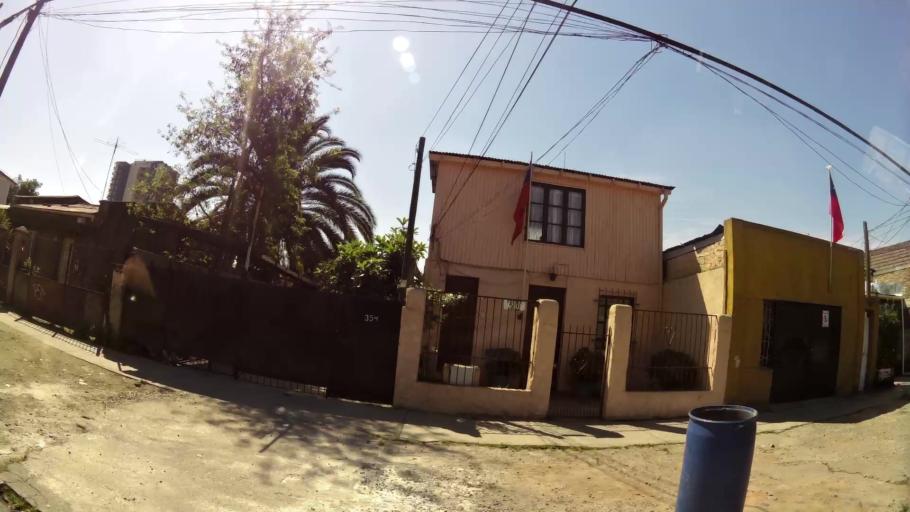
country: CL
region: Santiago Metropolitan
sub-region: Provincia de Santiago
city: Santiago
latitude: -33.5214
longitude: -70.6558
